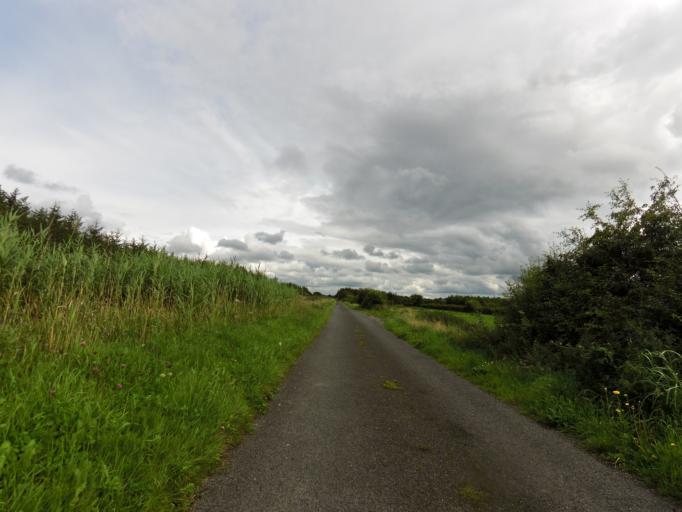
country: IE
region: Leinster
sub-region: An Iarmhi
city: An Muileann gCearr
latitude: 53.5666
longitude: -7.5116
